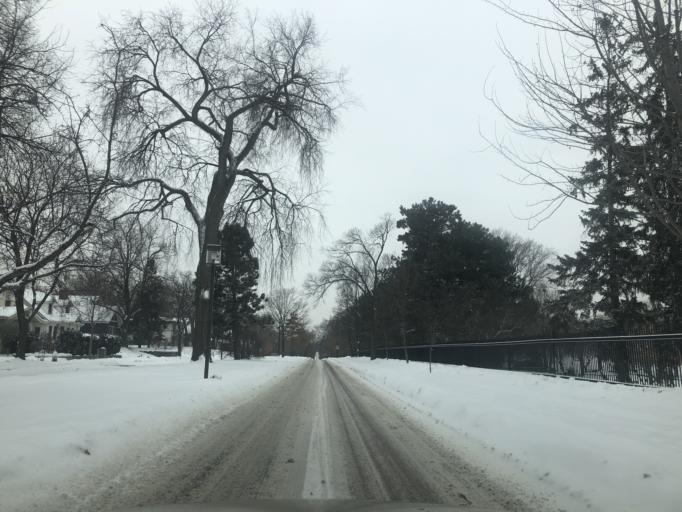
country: US
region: Minnesota
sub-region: Hennepin County
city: Minneapolis
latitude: 44.9368
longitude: -93.2935
